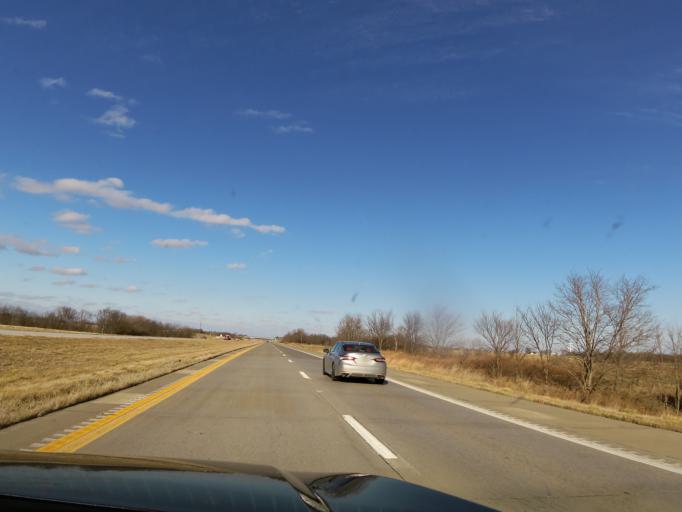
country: US
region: Missouri
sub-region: Lewis County
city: Canton
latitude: 40.0364
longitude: -91.5254
